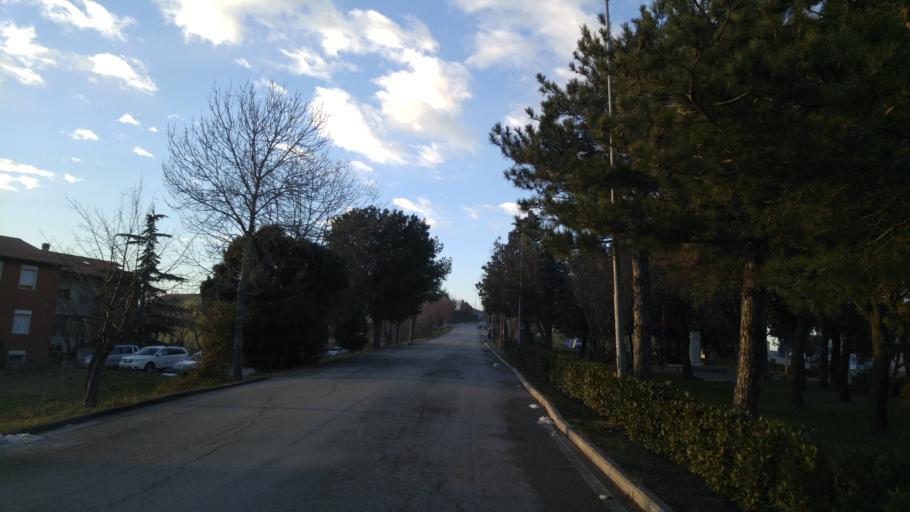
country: IT
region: The Marches
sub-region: Provincia di Pesaro e Urbino
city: San Giorgio di Pesaro
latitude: 43.7153
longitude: 12.9838
